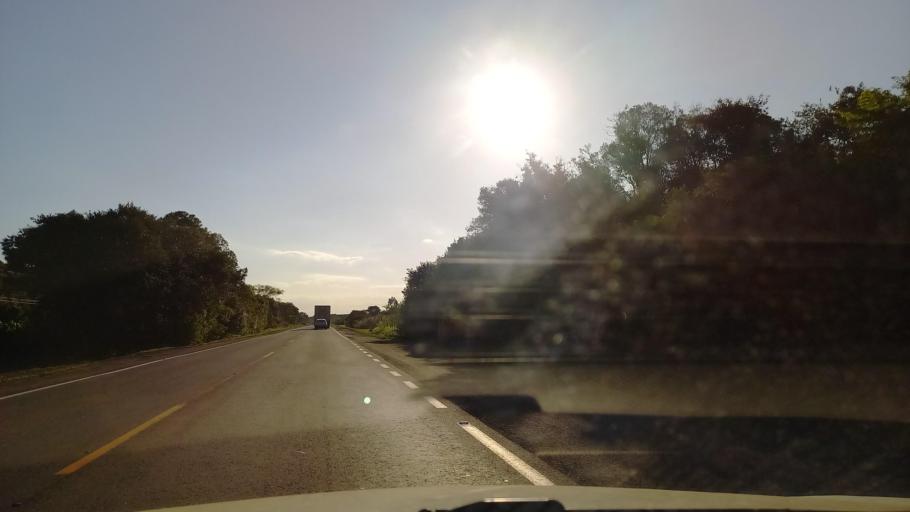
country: BR
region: Rio Grande do Sul
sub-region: Venancio Aires
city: Venancio Aires
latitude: -29.6653
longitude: -52.0532
